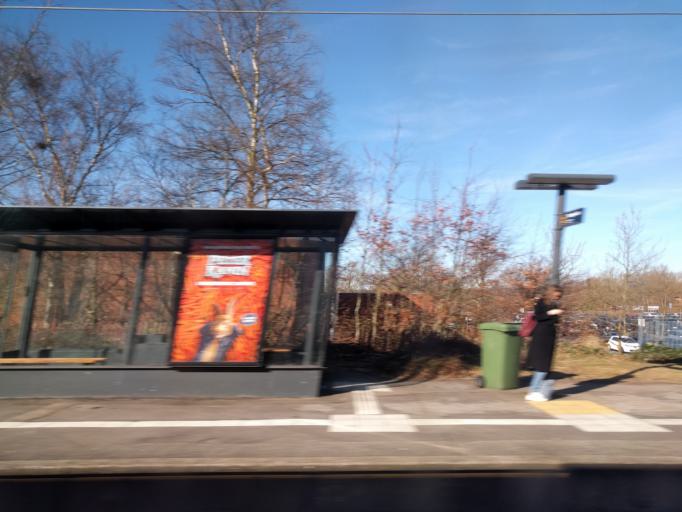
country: DK
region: Capital Region
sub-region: Rudersdal Kommune
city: Trorod
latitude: 55.8535
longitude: 12.5605
